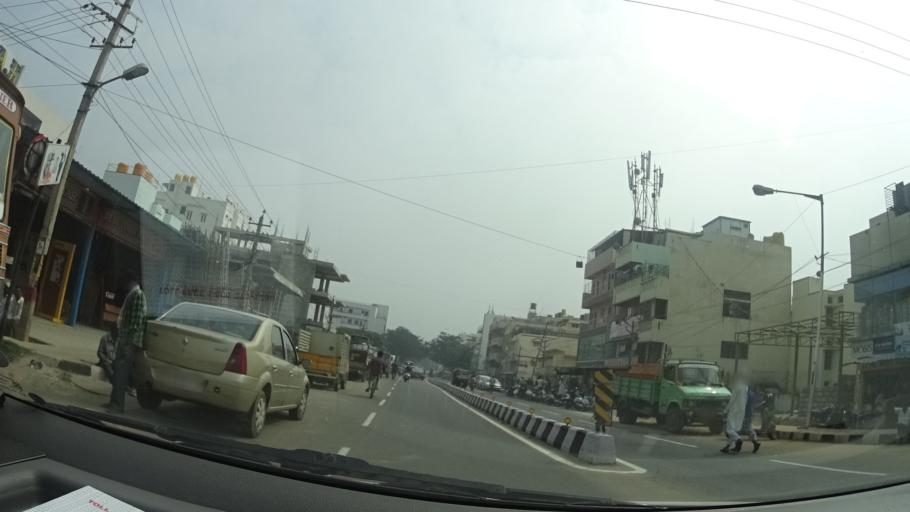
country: IN
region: Karnataka
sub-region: Bangalore Urban
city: Bangalore
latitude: 13.0269
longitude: 77.6210
